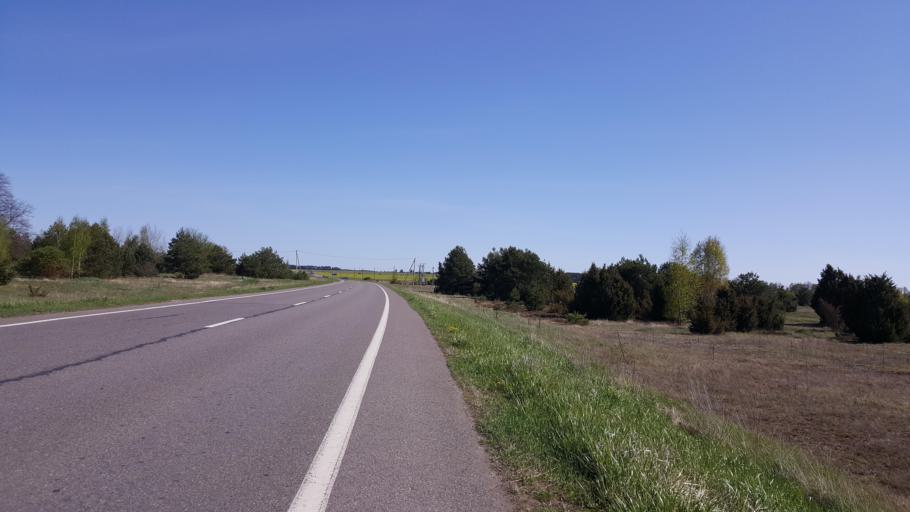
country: BY
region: Brest
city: Kamyanyets
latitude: 52.4249
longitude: 23.8387
